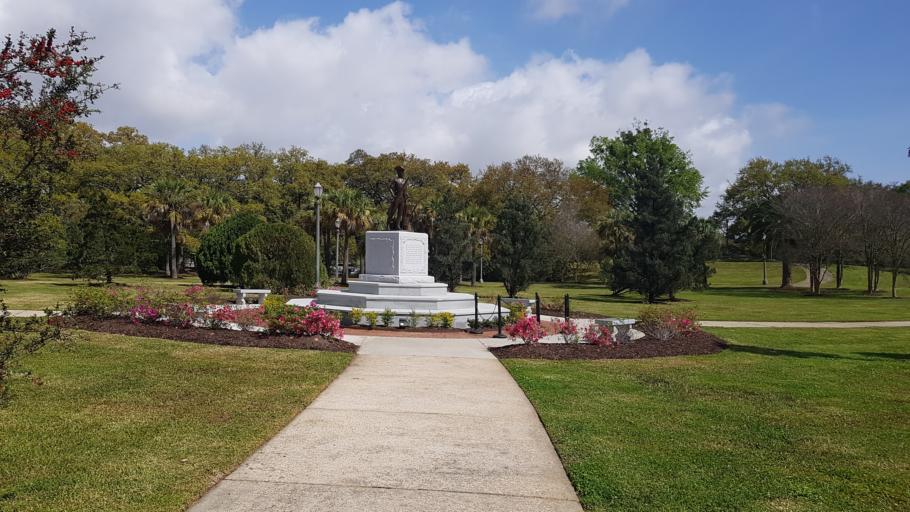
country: US
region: Louisiana
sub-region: West Baton Rouge Parish
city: Port Allen
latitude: 30.4576
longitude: -91.1856
